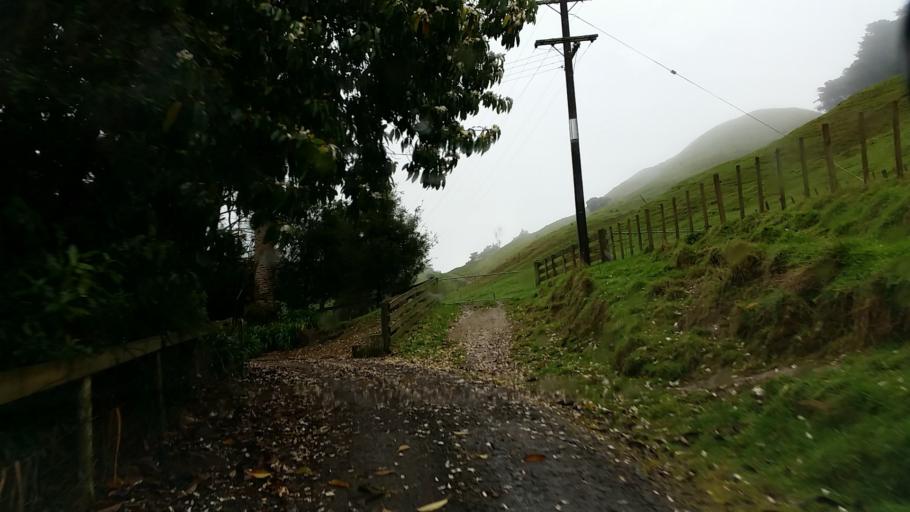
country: NZ
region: Taranaki
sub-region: South Taranaki District
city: Eltham
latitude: -39.4702
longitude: 174.4198
